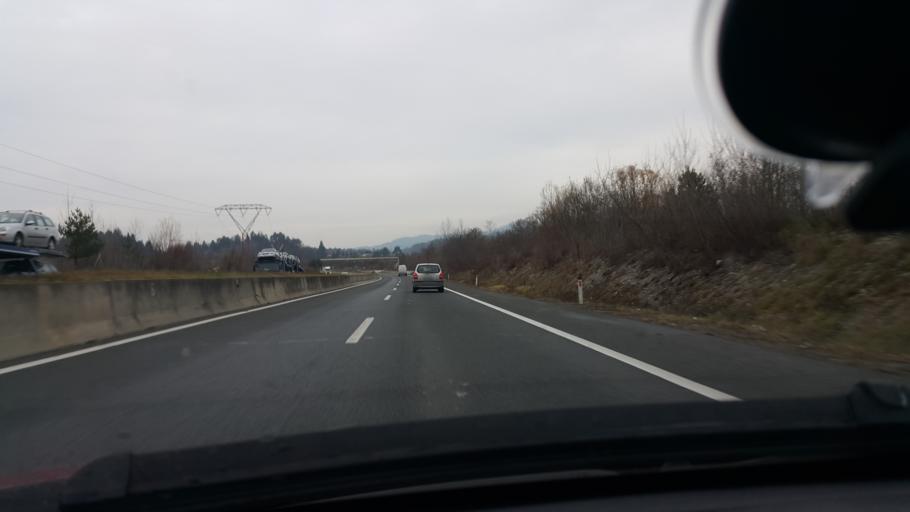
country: AT
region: Carinthia
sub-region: Politischer Bezirk Klagenfurt Land
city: Poggersdorf
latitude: 46.6453
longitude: 14.4171
